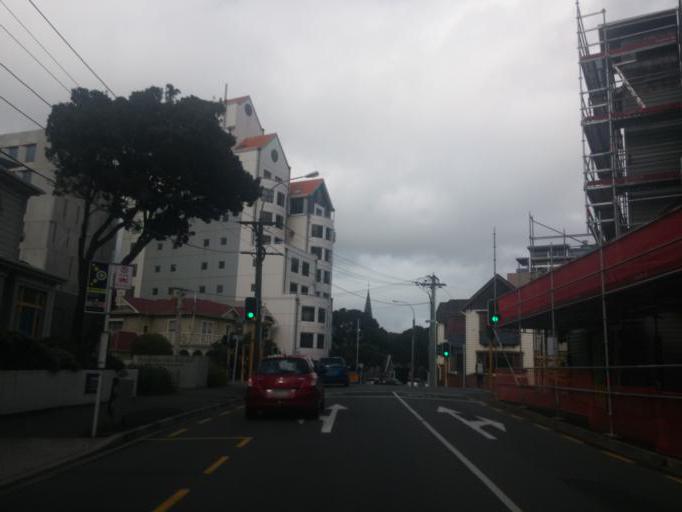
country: NZ
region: Wellington
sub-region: Wellington City
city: Wellington
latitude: -41.2753
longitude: 174.7796
